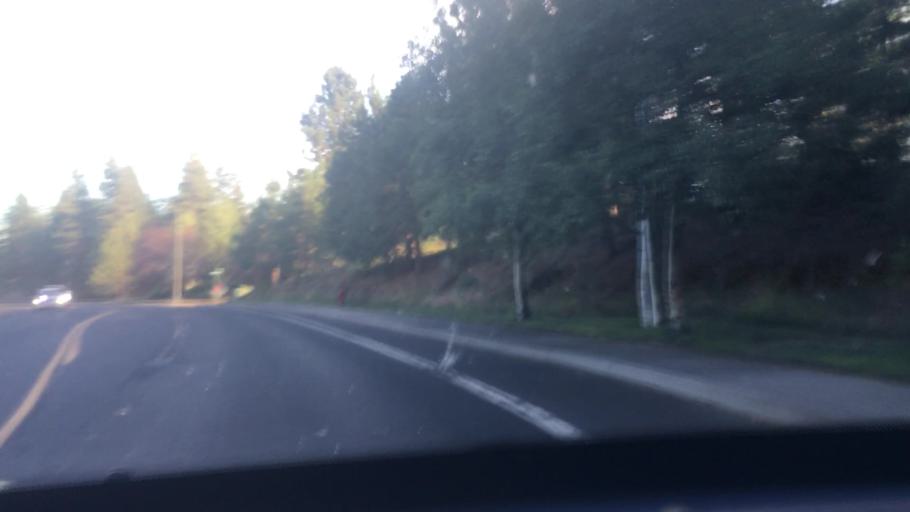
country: US
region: Oregon
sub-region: Deschutes County
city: Bend
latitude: 44.0424
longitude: -121.3438
